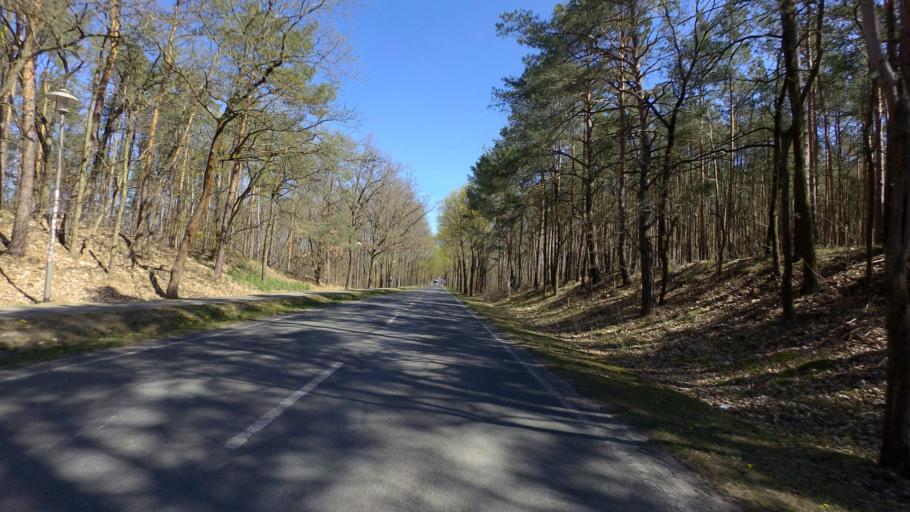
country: DE
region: Brandenburg
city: Zeuthen
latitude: 52.3441
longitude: 13.6194
